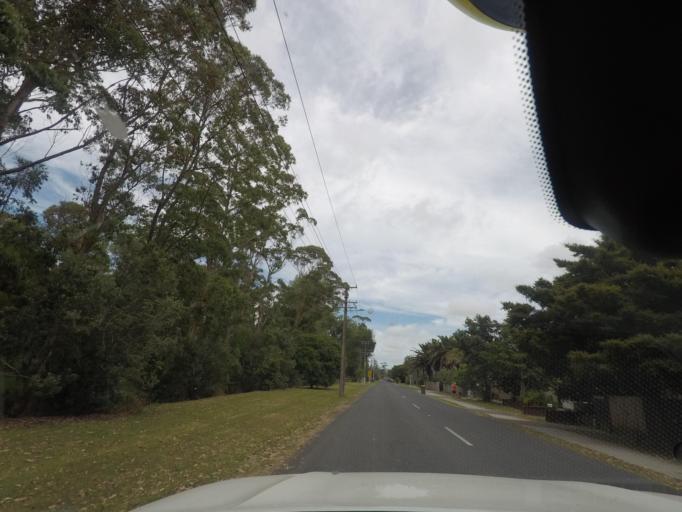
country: NZ
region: Auckland
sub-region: Auckland
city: Parakai
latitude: -36.6581
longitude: 174.4349
